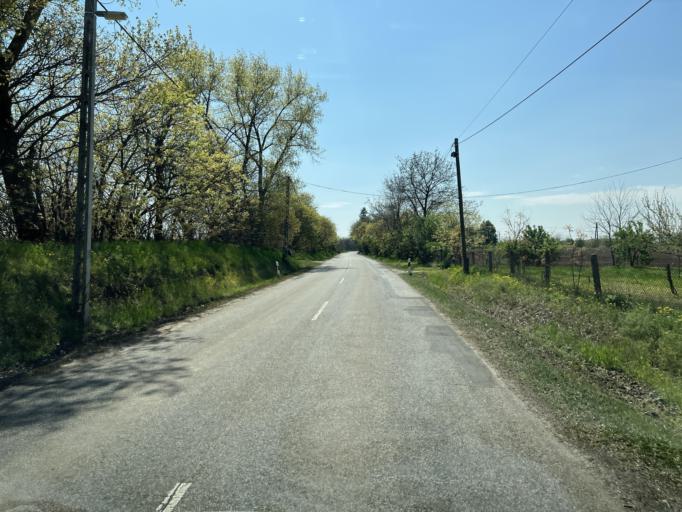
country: HU
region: Pest
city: Inarcs
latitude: 47.2434
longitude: 19.3169
